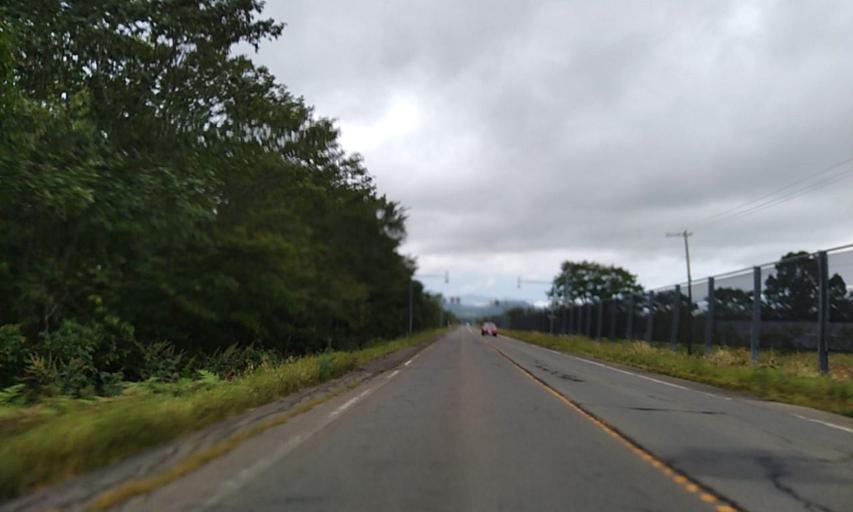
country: JP
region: Hokkaido
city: Bihoro
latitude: 43.5127
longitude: 144.4425
